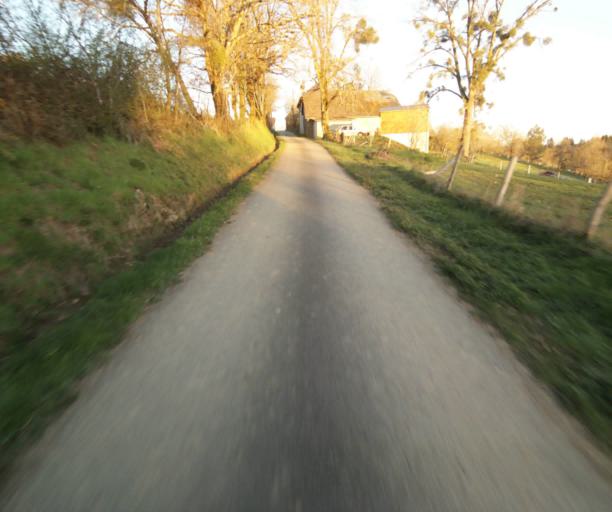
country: FR
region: Limousin
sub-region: Departement de la Correze
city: Saint-Mexant
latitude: 45.2944
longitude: 1.6032
